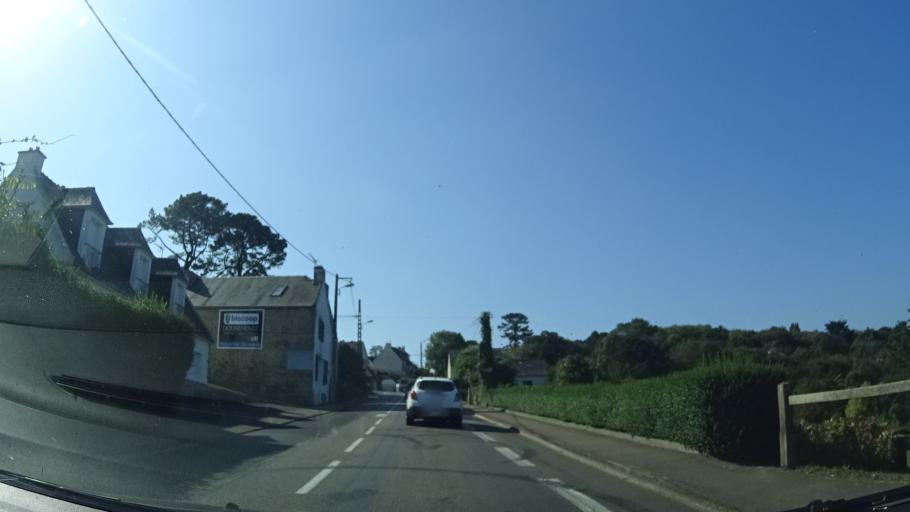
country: FR
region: Brittany
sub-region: Departement du Finistere
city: Douarnenez
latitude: 48.0889
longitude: -4.3038
